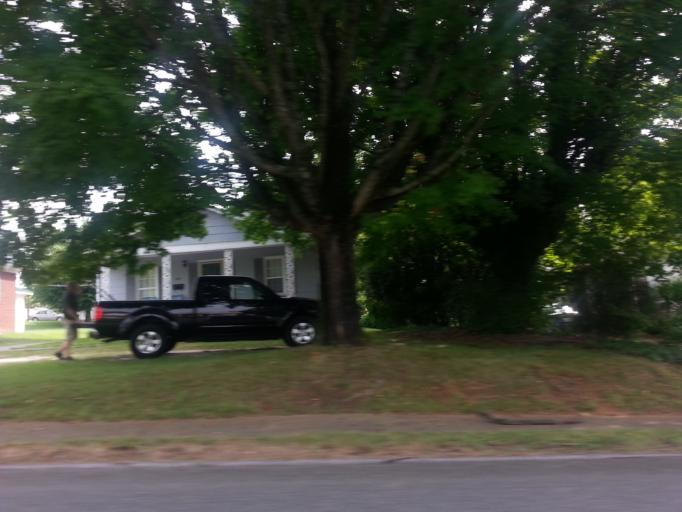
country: US
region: Tennessee
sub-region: Blount County
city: Maryville
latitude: 35.7678
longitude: -83.9566
